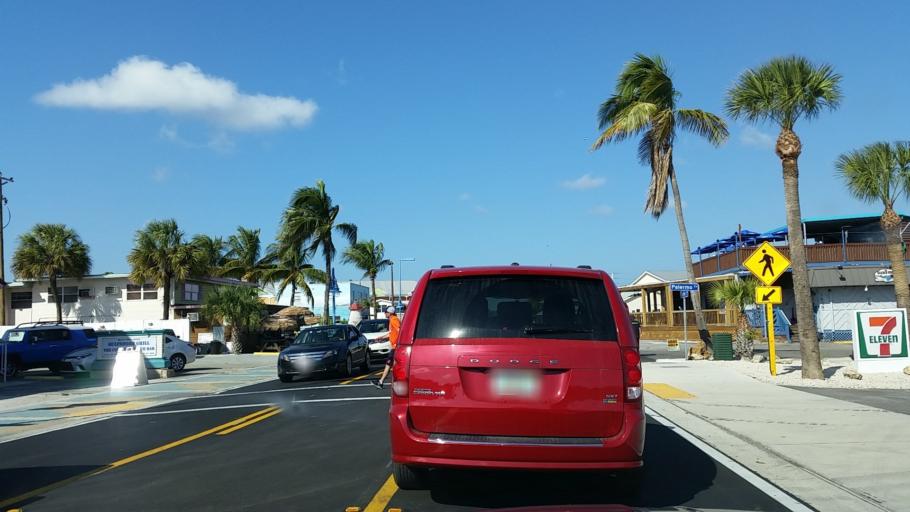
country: US
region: Florida
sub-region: Lee County
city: Fort Myers Beach
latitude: 26.4519
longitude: -81.9521
